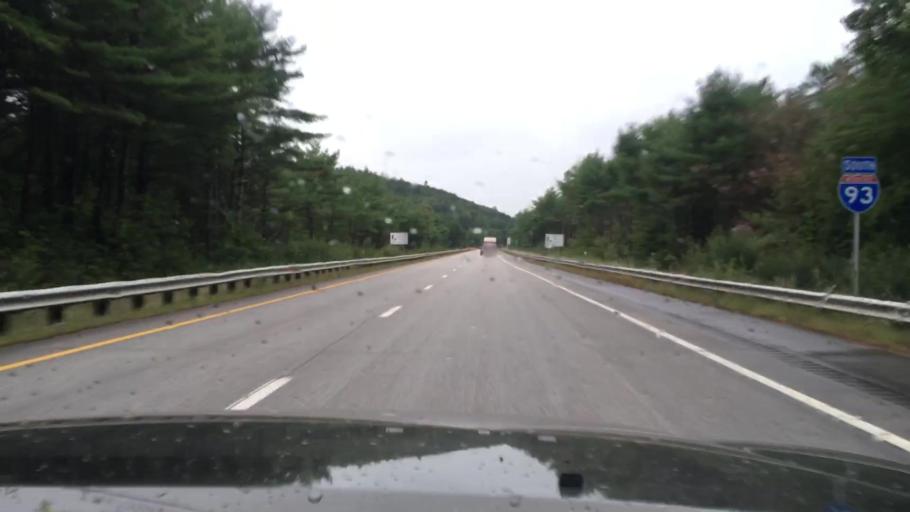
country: US
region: New Hampshire
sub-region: Merrimack County
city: Northfield
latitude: 43.4241
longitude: -71.5918
